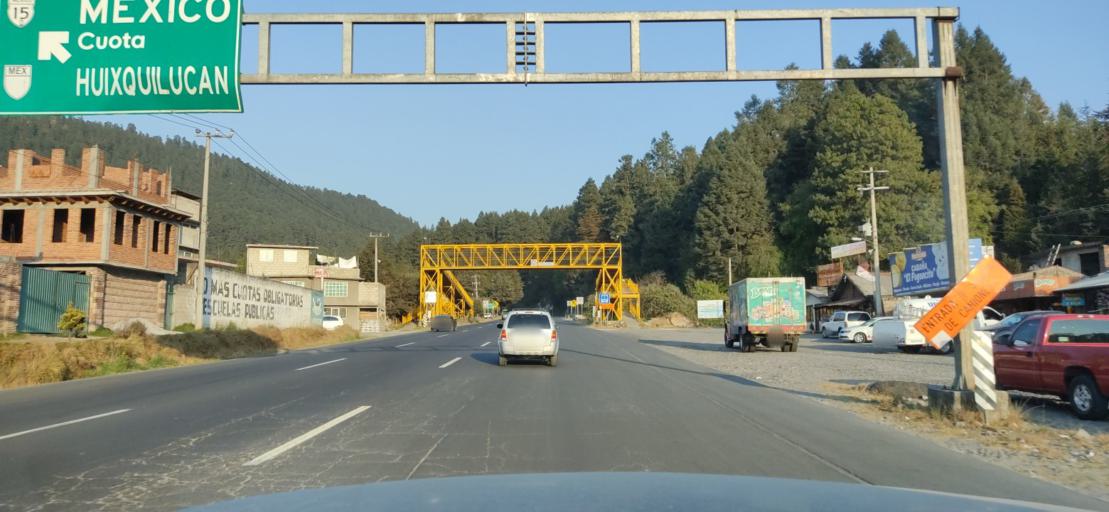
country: MX
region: Mexico City
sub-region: Cuajimalpa de Morelos
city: San Lorenzo Acopilco
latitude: 19.2976
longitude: -99.3697
